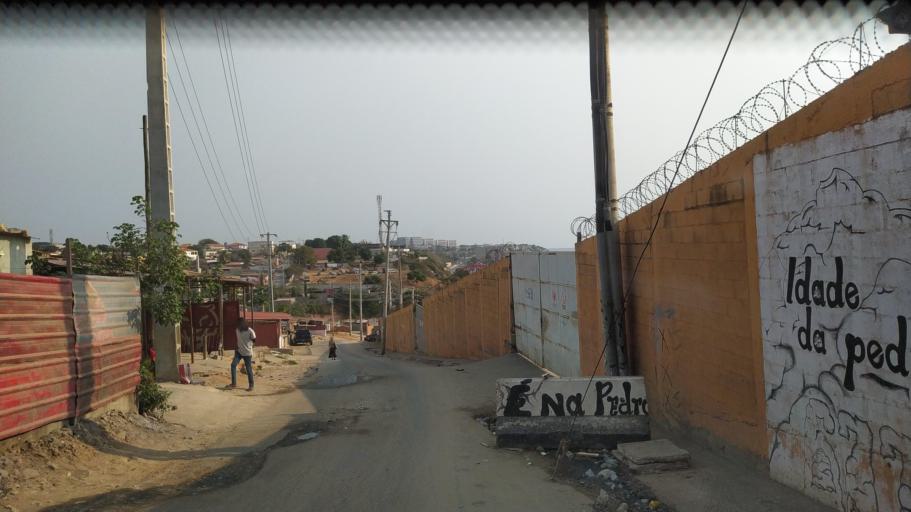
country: AO
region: Luanda
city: Luanda
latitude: -8.8700
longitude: 13.1988
